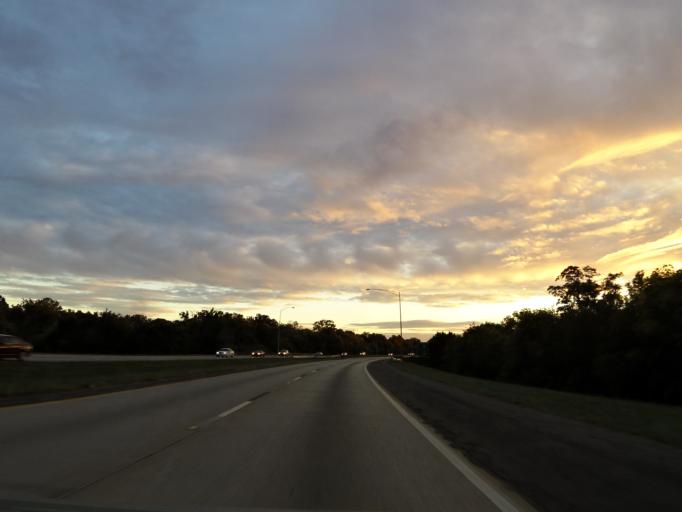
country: US
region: Alabama
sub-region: Jefferson County
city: Irondale
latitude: 33.5712
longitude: -86.7189
